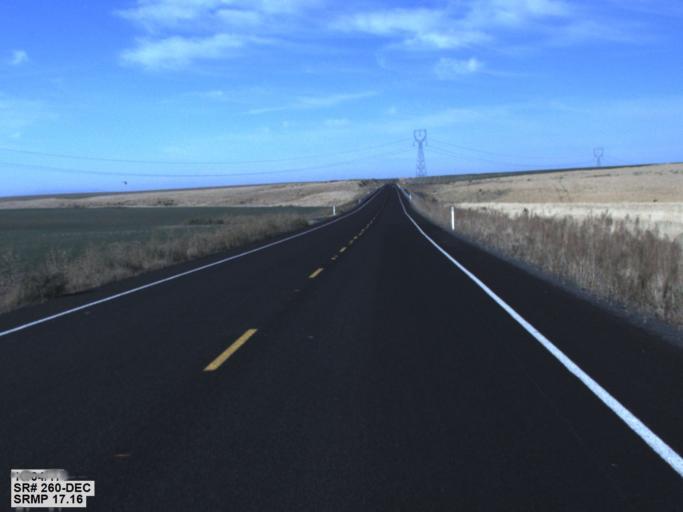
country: US
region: Washington
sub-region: Franklin County
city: Connell
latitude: 46.6202
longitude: -118.6970
